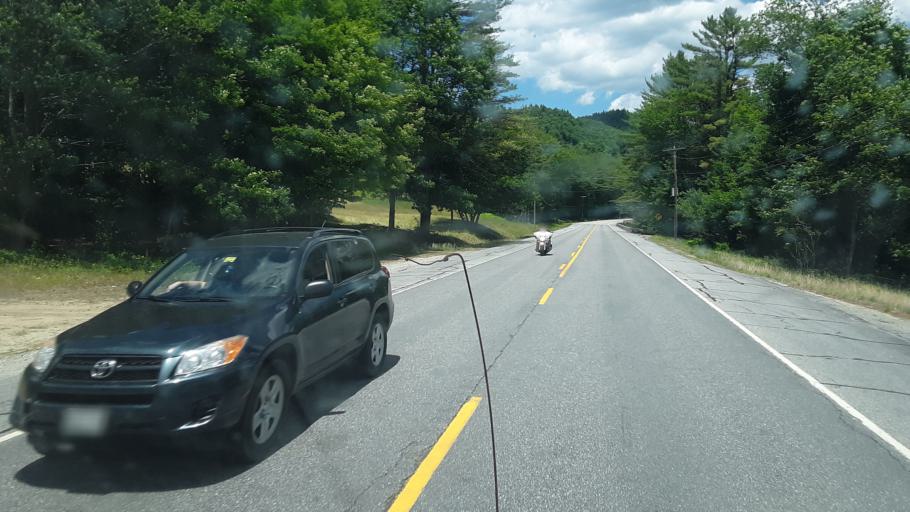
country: US
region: Maine
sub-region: Oxford County
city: Rumford
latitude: 44.4946
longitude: -70.6409
